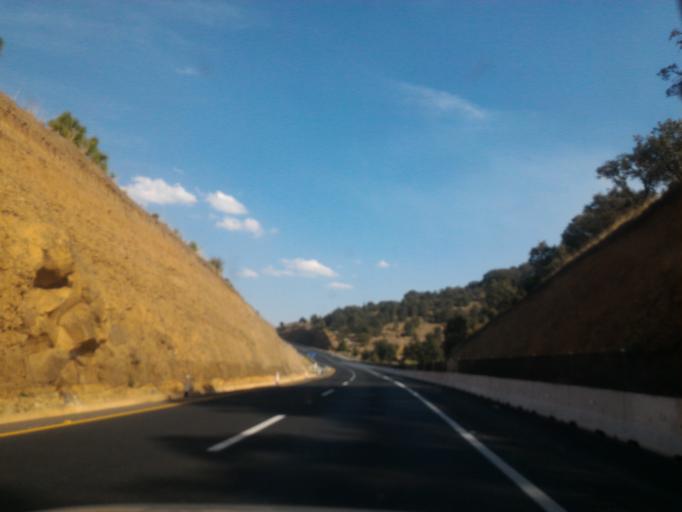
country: MX
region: Mexico
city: Temascalcingo de Jose Maria Velazco
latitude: 19.8529
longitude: -100.0165
